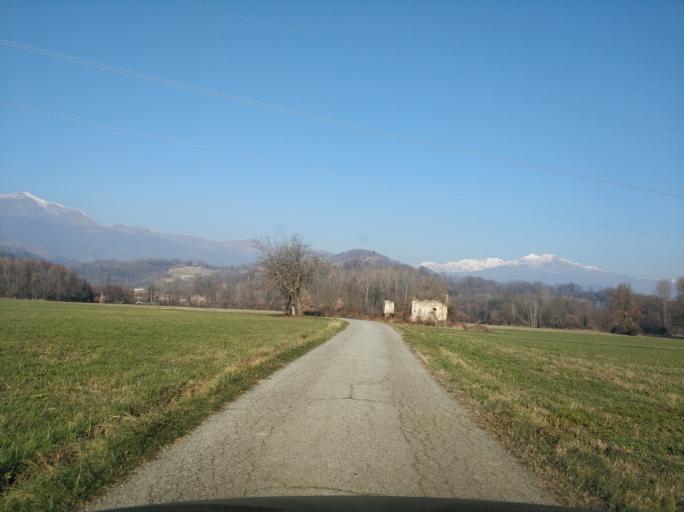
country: IT
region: Piedmont
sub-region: Provincia di Torino
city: Levone
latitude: 45.3124
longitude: 7.6147
